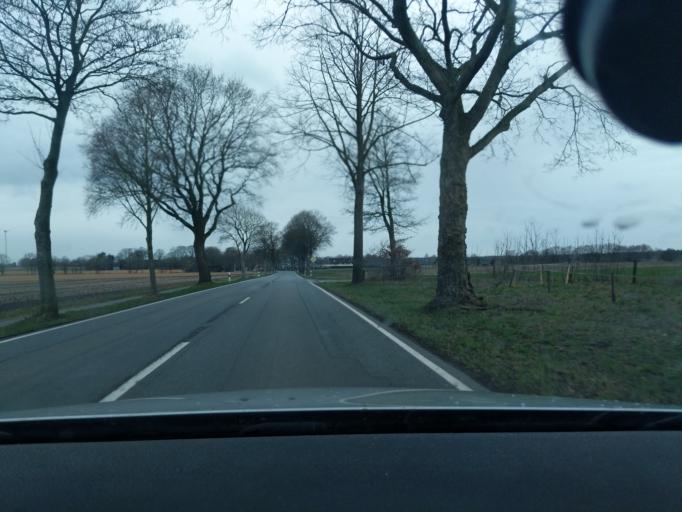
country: DE
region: Lower Saxony
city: Kutenholz
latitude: 53.4910
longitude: 9.2886
